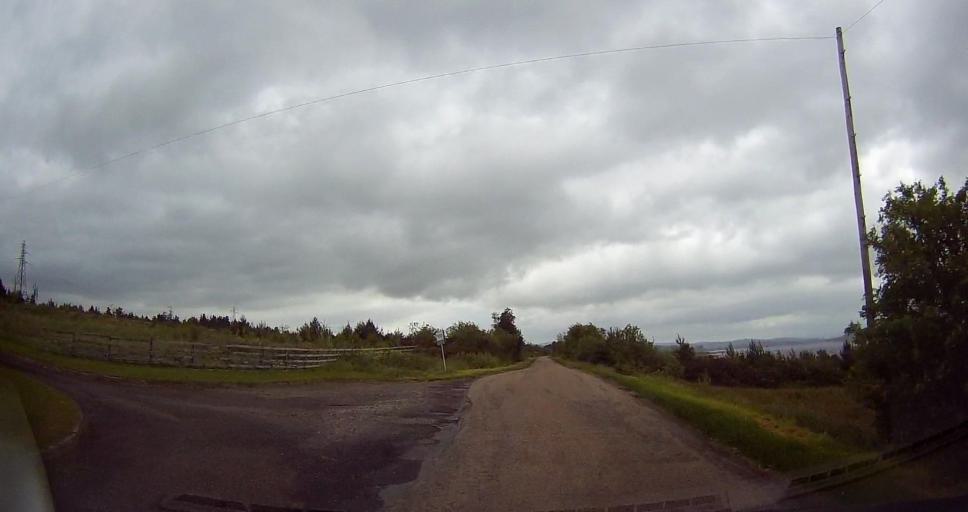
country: GB
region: Scotland
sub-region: Highland
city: Evanton
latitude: 58.0700
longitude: -4.4573
